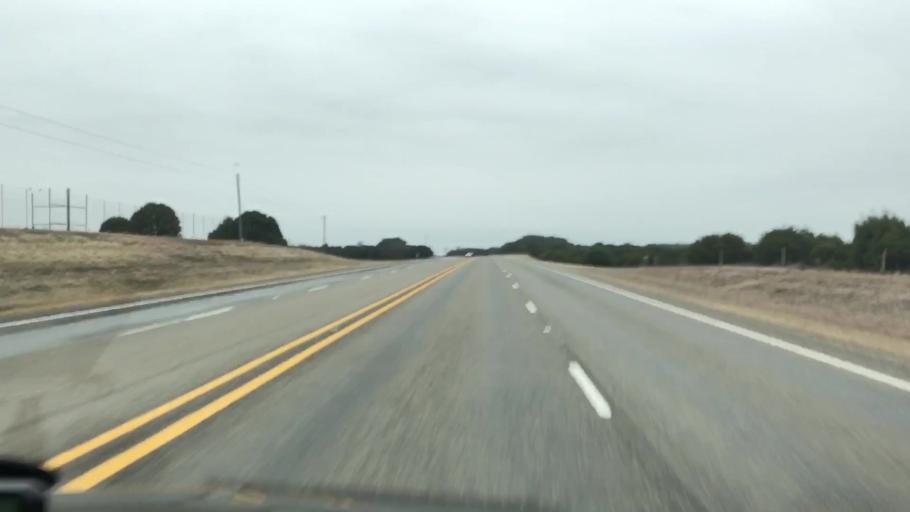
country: US
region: Texas
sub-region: Lampasas County
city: Lampasas
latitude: 31.1859
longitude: -98.1723
